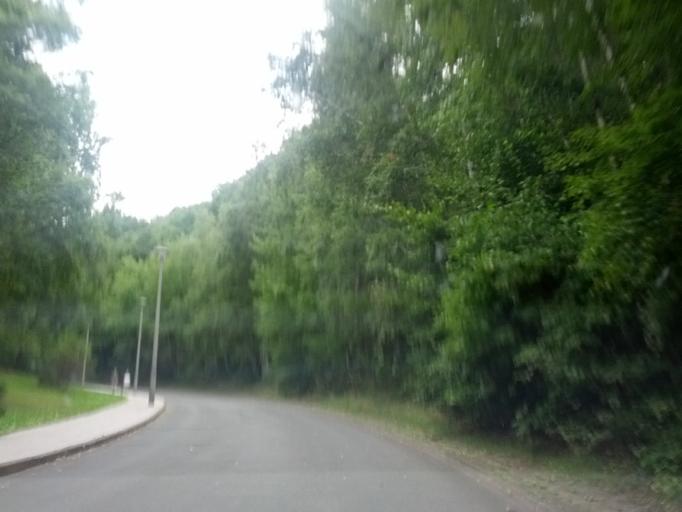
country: DE
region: Thuringia
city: Friedrichroda
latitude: 50.8643
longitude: 10.5725
